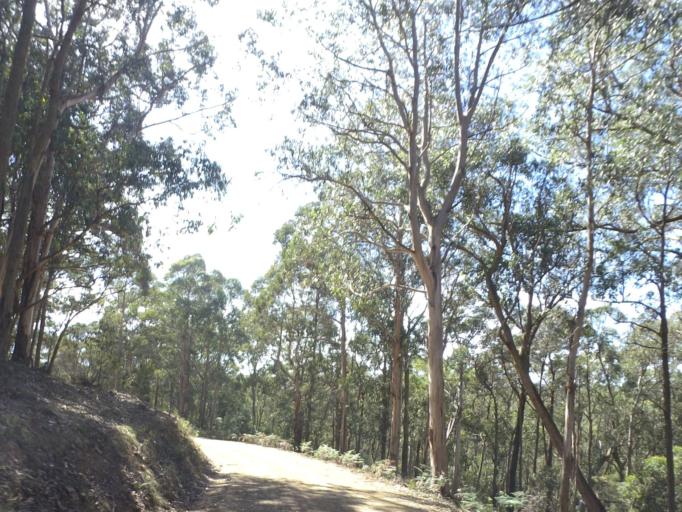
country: AU
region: Victoria
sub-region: Moorabool
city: Bacchus Marsh
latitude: -37.4340
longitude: 144.3539
